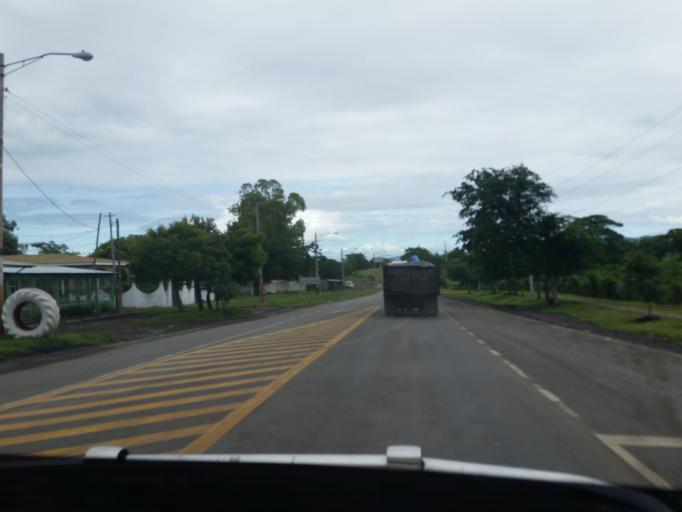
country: NI
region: Managua
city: Tipitapa
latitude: 12.3108
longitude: -86.0545
